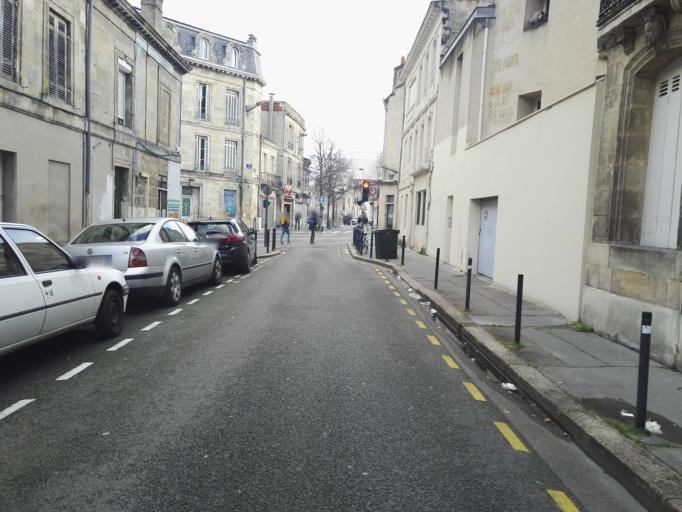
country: FR
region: Aquitaine
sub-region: Departement de la Gironde
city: Bordeaux
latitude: 44.8279
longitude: -0.5756
